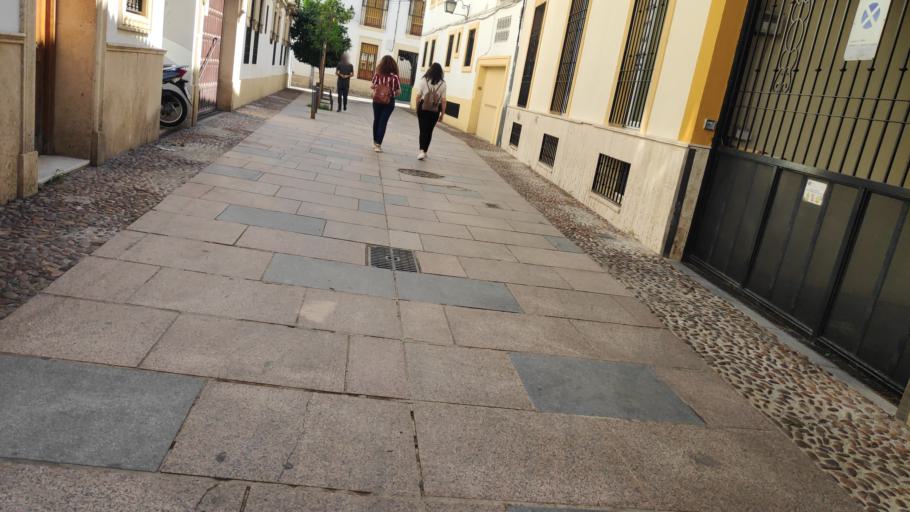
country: ES
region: Andalusia
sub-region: Province of Cordoba
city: Cordoba
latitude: 37.8847
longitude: -4.7740
